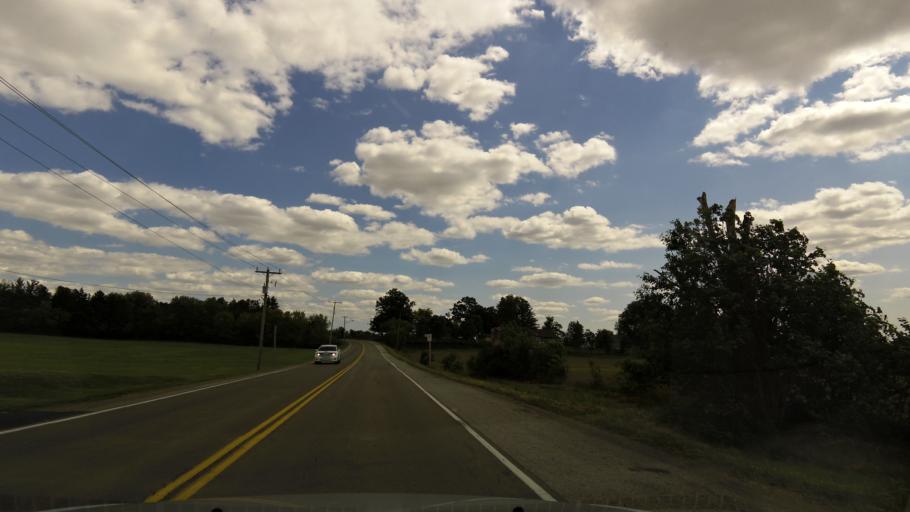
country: CA
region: Ontario
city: Ancaster
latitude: 43.1760
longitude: -80.0365
